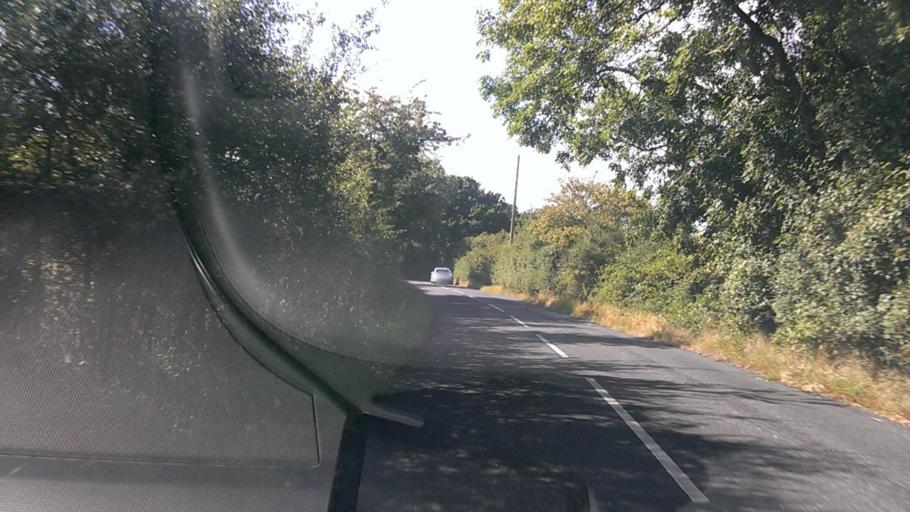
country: GB
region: England
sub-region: Essex
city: Layer de la Haye
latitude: 51.8384
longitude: 0.9020
